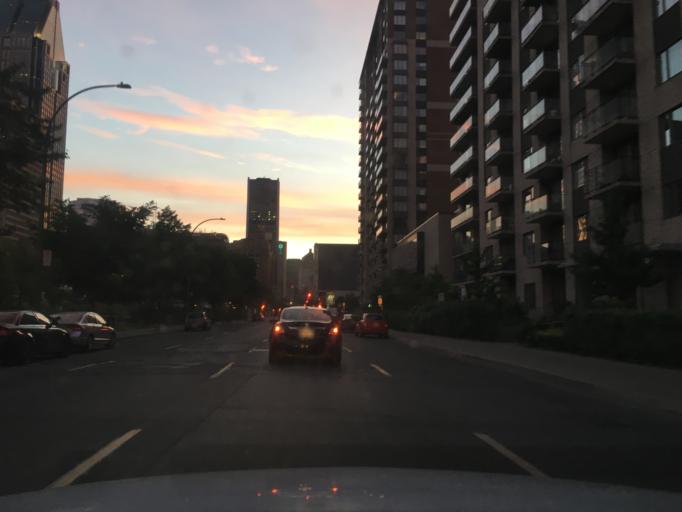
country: CA
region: Quebec
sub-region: Montreal
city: Montreal
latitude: 45.4941
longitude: -73.5673
